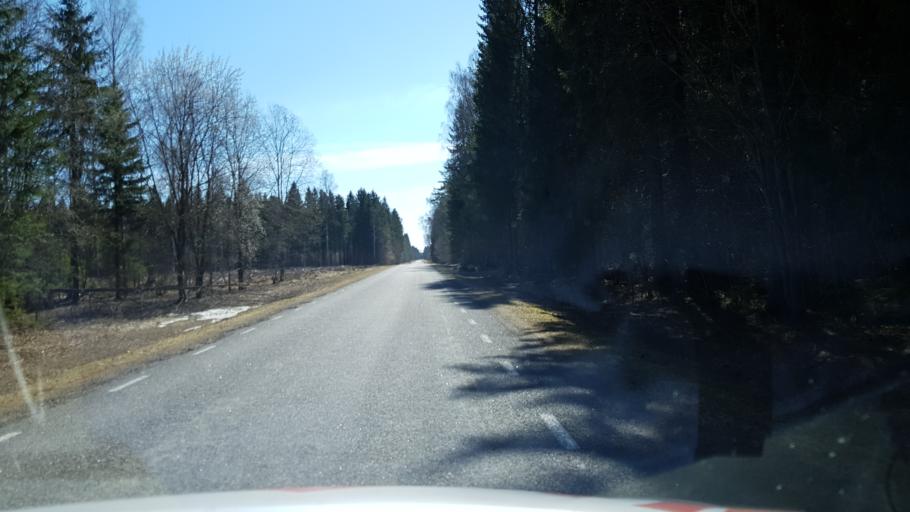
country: EE
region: Laeaene-Virumaa
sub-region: Vinni vald
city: Vinni
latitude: 59.1524
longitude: 26.5177
